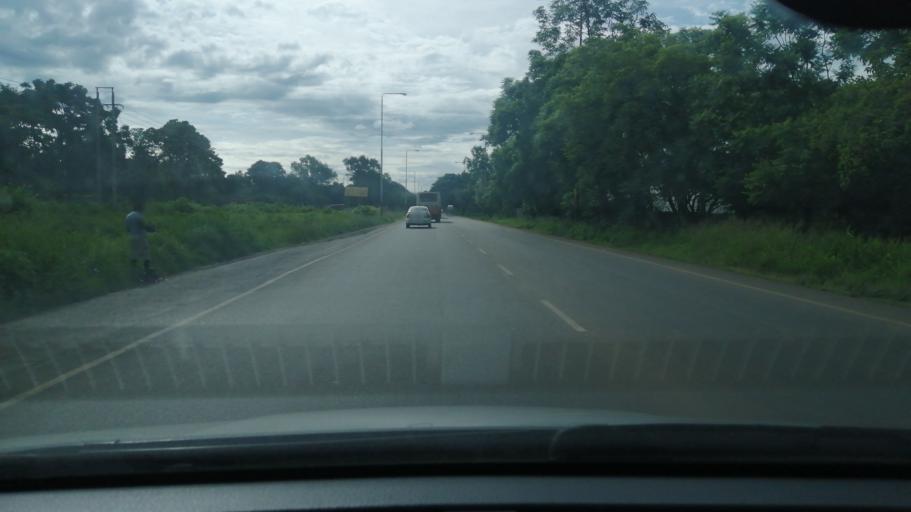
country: ZW
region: Harare
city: Harare
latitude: -17.7642
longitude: 30.9925
